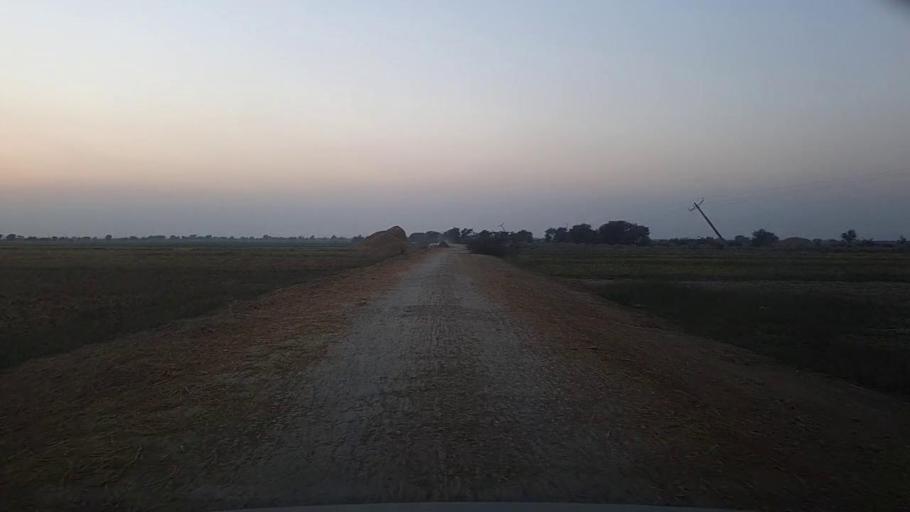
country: PK
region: Sindh
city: Khairpur Nathan Shah
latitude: 27.1809
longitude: 67.6094
